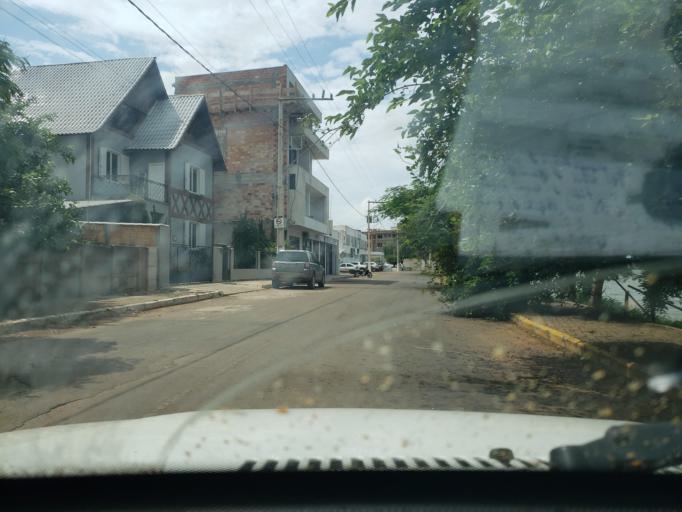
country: BR
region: Minas Gerais
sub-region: Boa Esperanca
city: Boa Esperanca
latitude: -21.0855
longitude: -45.5706
